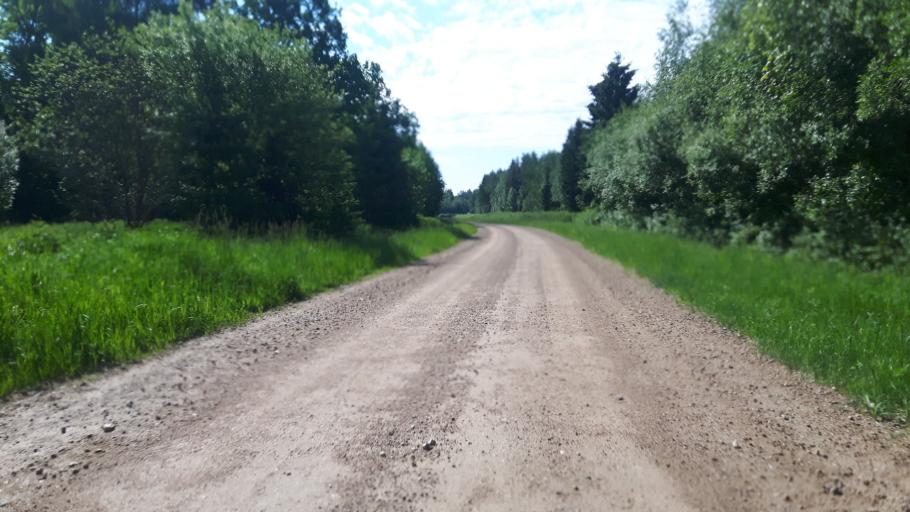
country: EE
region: Paernumaa
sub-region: Vaendra vald (alev)
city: Vandra
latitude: 58.6963
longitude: 25.0310
